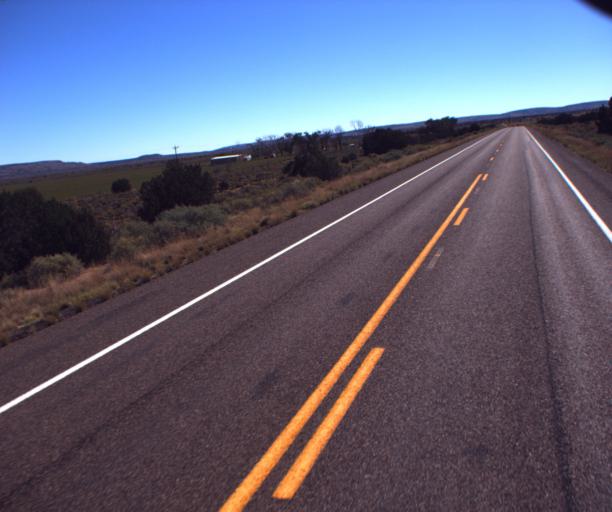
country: US
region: Arizona
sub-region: Apache County
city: Saint Johns
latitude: 34.6189
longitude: -109.6607
